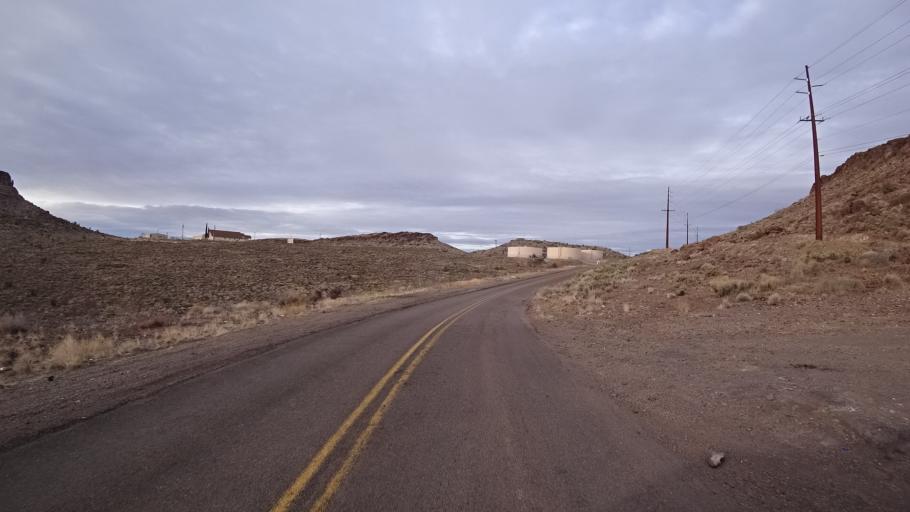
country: US
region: Arizona
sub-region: Mohave County
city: Kingman
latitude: 35.2175
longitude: -114.0613
